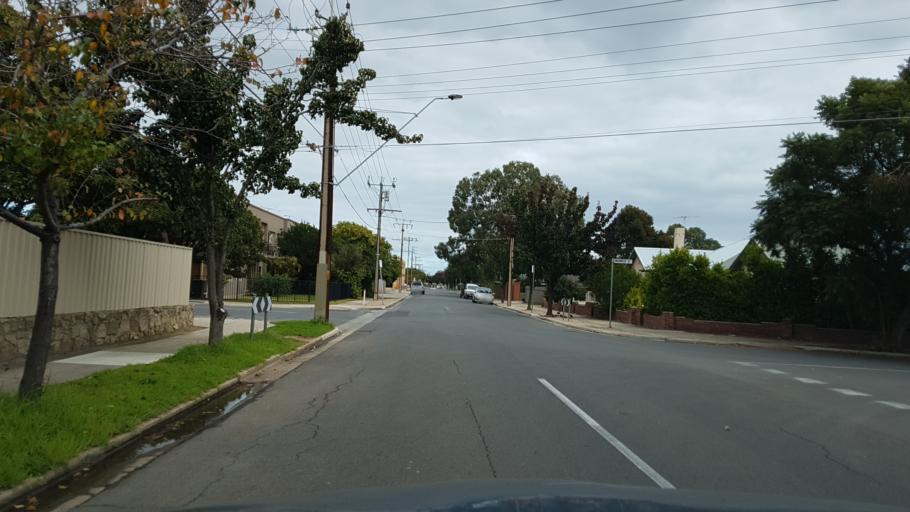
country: AU
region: South Australia
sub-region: Unley
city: Forestville
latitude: -34.9547
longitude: 138.5664
